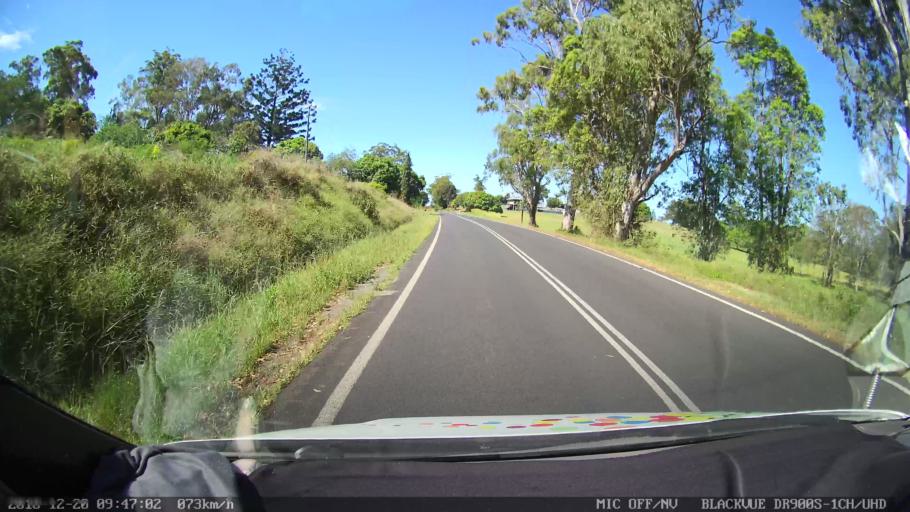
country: AU
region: New South Wales
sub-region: Lismore Municipality
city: Lismore
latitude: -28.7593
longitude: 153.3002
